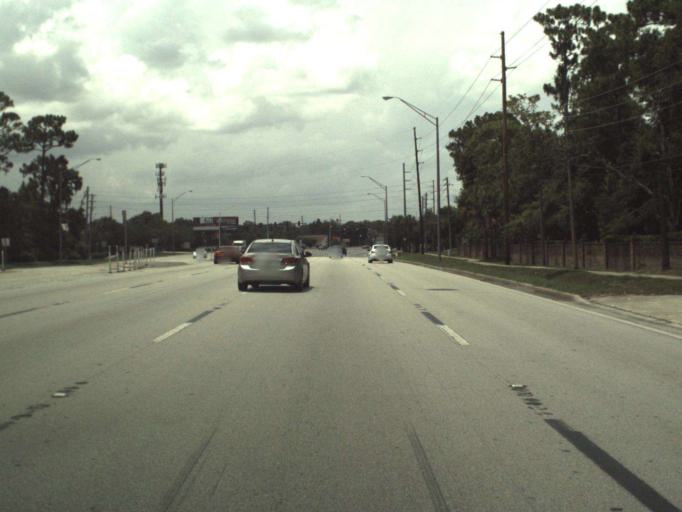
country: US
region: Florida
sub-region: Seminole County
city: Fern Park
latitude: 28.6369
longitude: -81.3211
